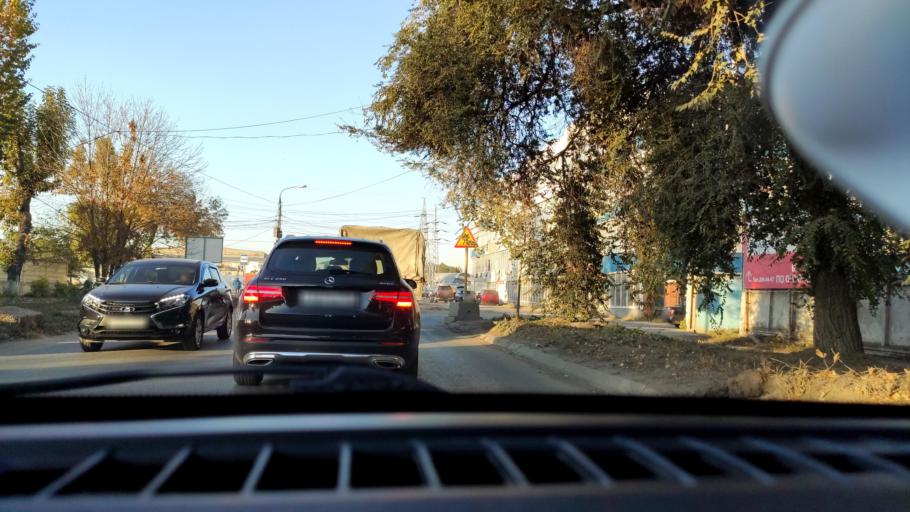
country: RU
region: Samara
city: Samara
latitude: 53.1939
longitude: 50.2456
